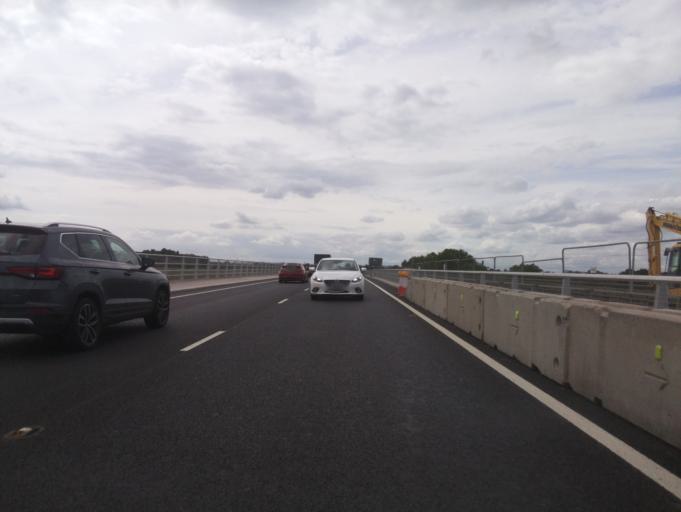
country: GB
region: England
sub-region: Worcestershire
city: Kempsey
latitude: 52.1634
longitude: -2.2302
